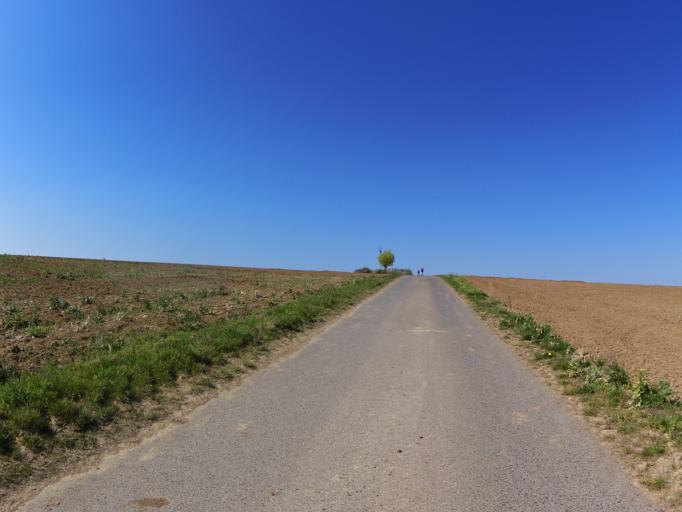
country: DE
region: Bavaria
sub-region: Regierungsbezirk Unterfranken
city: Rottendorf
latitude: 49.8146
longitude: 10.0772
